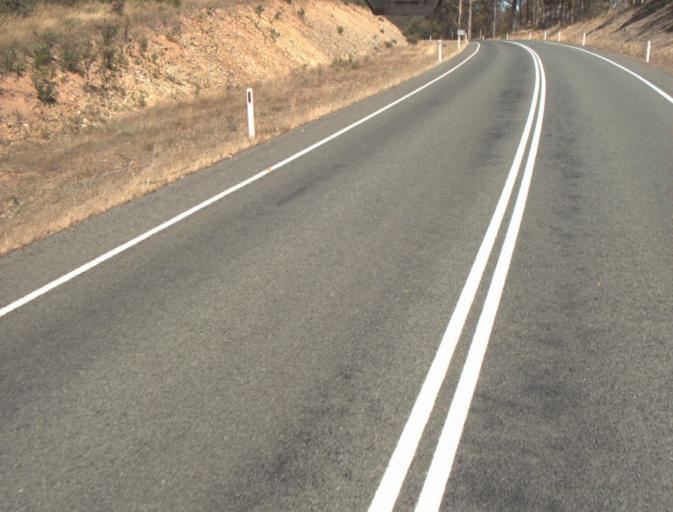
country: AU
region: Tasmania
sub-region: Launceston
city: Newstead
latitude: -41.3353
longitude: 147.3480
